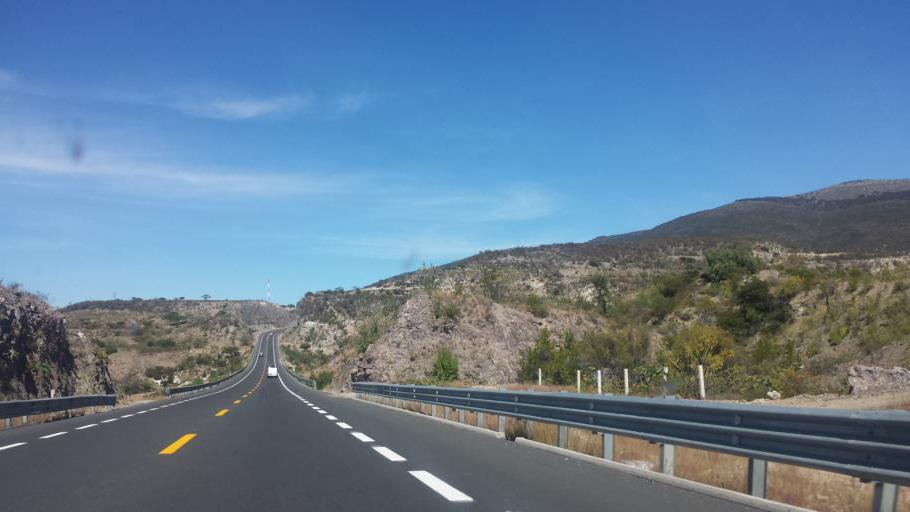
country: MX
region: Oaxaca
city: San Gabriel Casa Blanca
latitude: 17.9698
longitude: -97.3575
